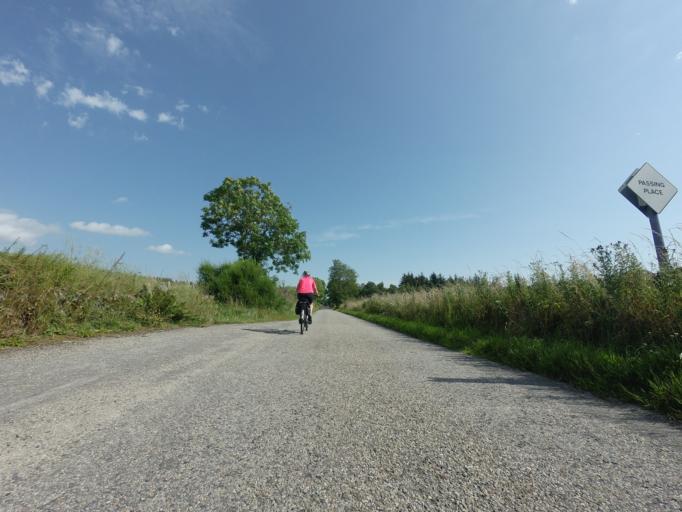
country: GB
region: Scotland
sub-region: Highland
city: Invergordon
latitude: 57.7260
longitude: -4.1967
